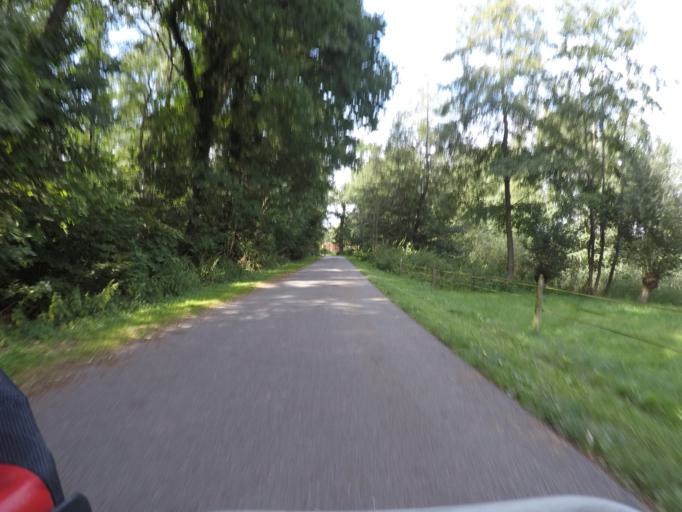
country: DE
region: Lower Saxony
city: Radbruch
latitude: 53.3635
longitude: 10.2983
